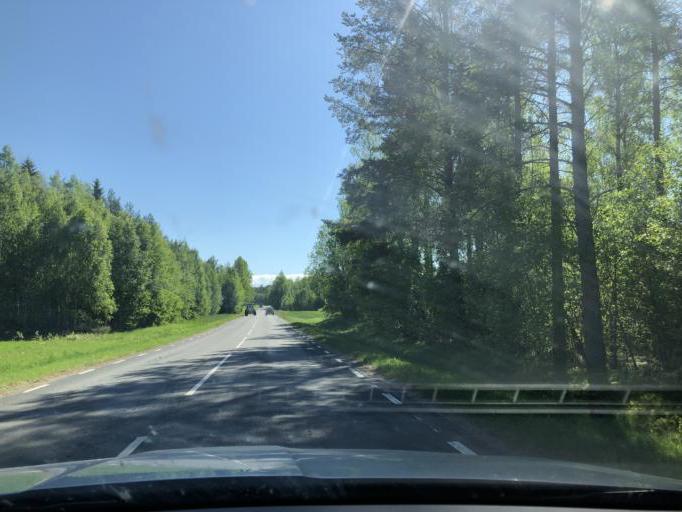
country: SE
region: Norrbotten
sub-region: Lulea Kommun
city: Gammelstad
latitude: 65.6609
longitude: 21.9813
